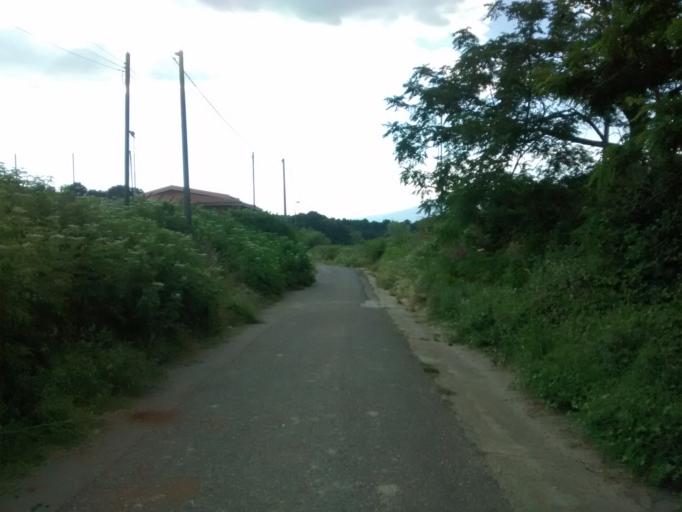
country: IT
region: Calabria
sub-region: Provincia di Catanzaro
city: Cortale
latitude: 38.8818
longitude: 16.4138
